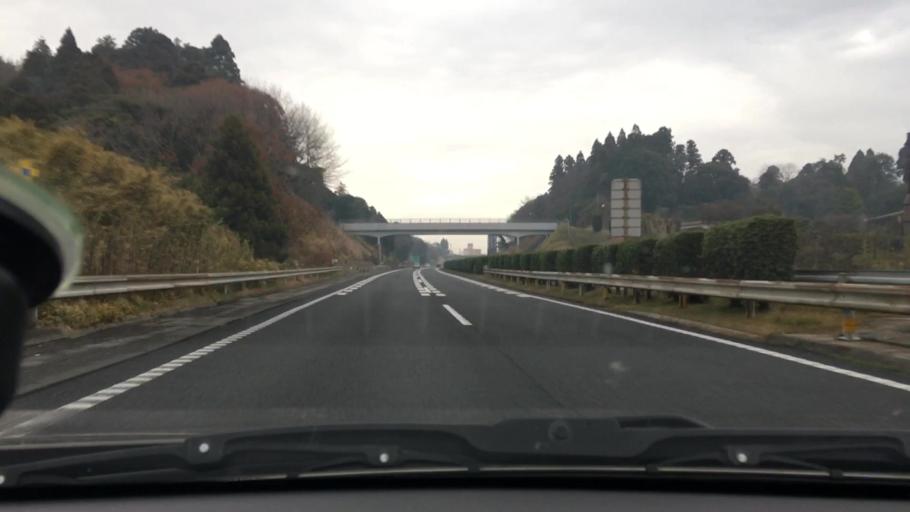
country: JP
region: Chiba
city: Narita
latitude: 35.7948
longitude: 140.3530
